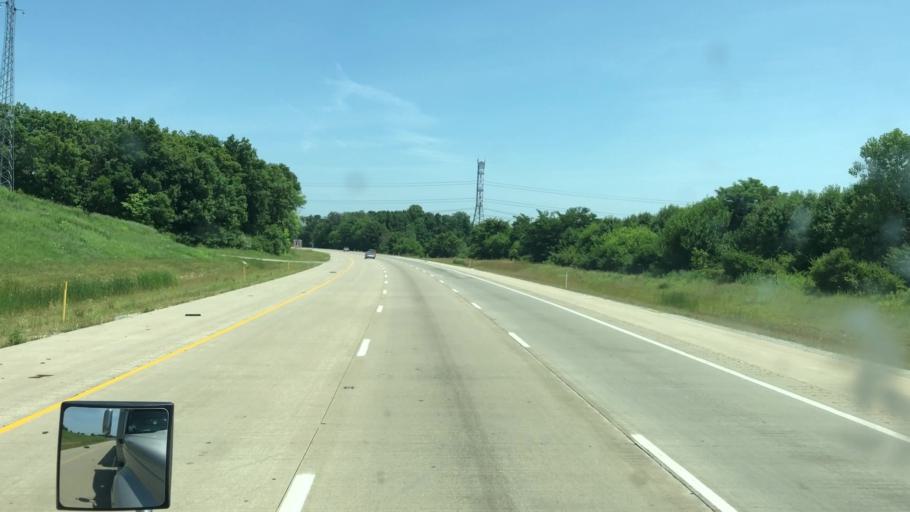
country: US
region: Indiana
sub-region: Marion County
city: Cumberland
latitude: 39.8034
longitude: -85.9656
